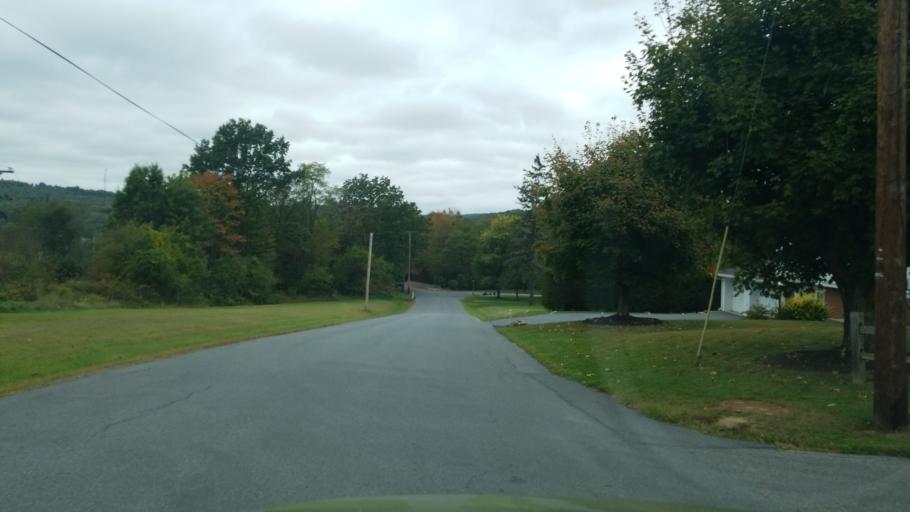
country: US
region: Pennsylvania
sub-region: Clearfield County
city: Curwensville
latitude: 40.9708
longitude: -78.5119
